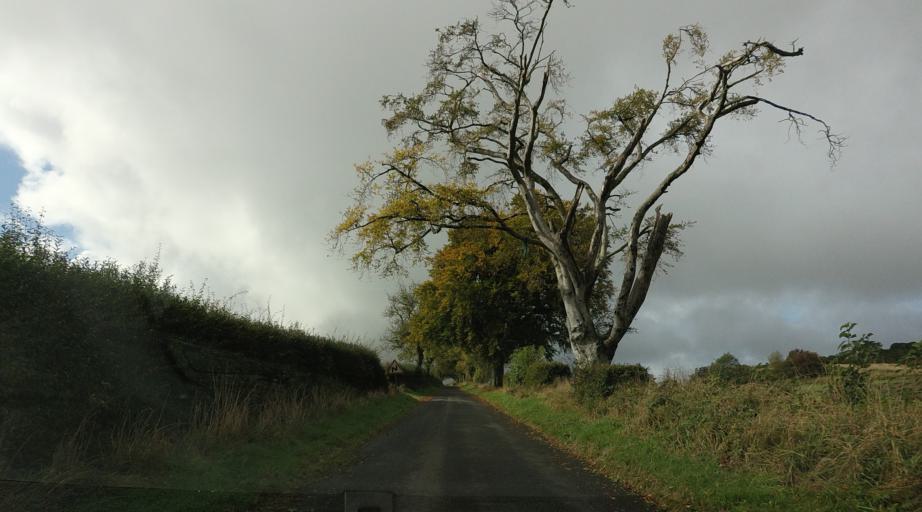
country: GB
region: Scotland
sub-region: Fife
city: Balmullo
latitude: 56.3604
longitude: -2.9556
